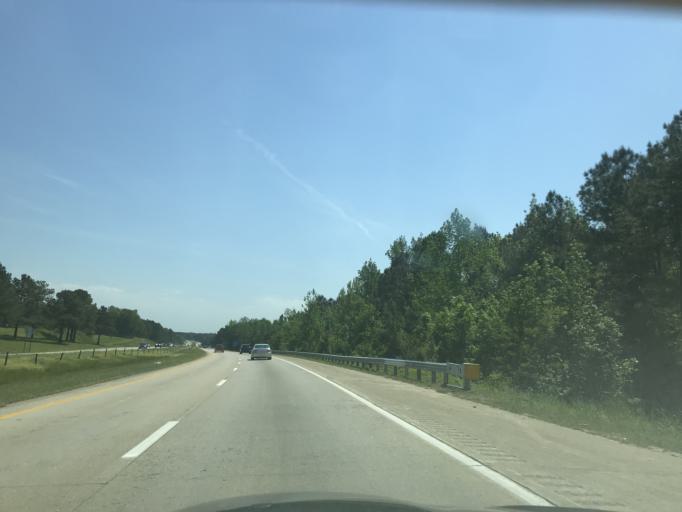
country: US
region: North Carolina
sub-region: Johnston County
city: Benson
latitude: 35.4407
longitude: -78.5346
